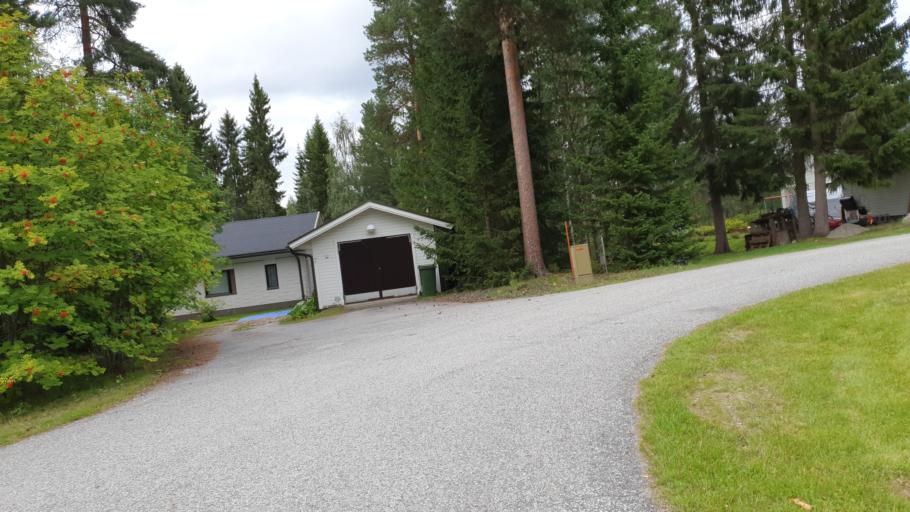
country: FI
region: Kainuu
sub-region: Kehys-Kainuu
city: Kuhmo
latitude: 64.1367
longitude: 29.4621
